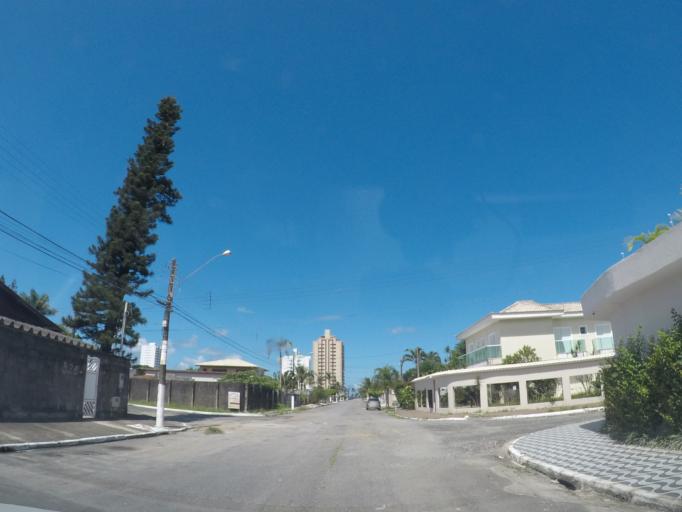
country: BR
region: Sao Paulo
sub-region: Mongagua
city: Mongagua
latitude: -24.0677
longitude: -46.5685
